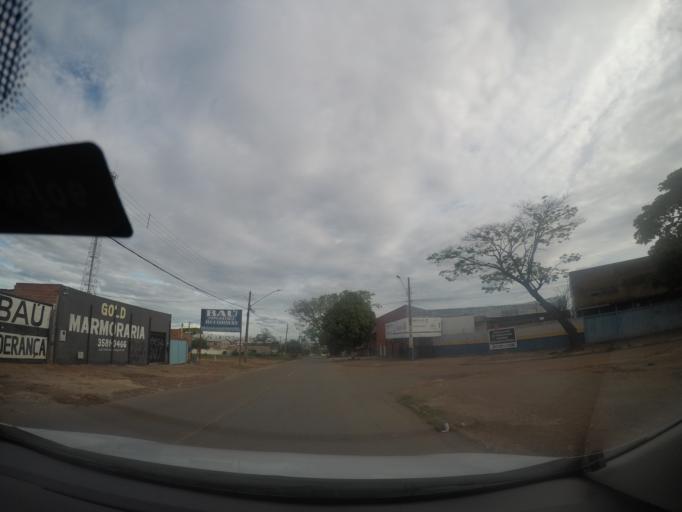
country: BR
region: Goias
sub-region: Goiania
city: Goiania
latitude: -16.6537
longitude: -49.3193
